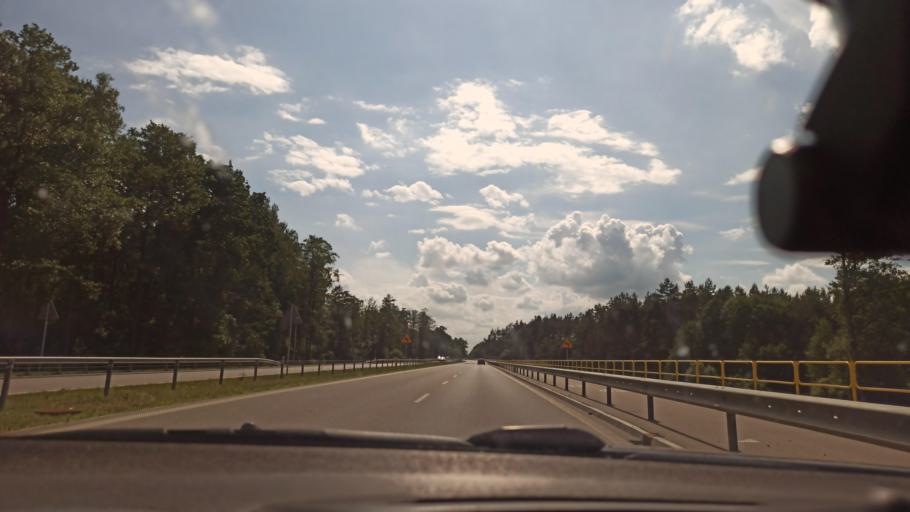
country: PL
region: Podlasie
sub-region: Powiat bialostocki
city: Turosn Koscielna
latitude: 53.0653
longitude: 23.0712
